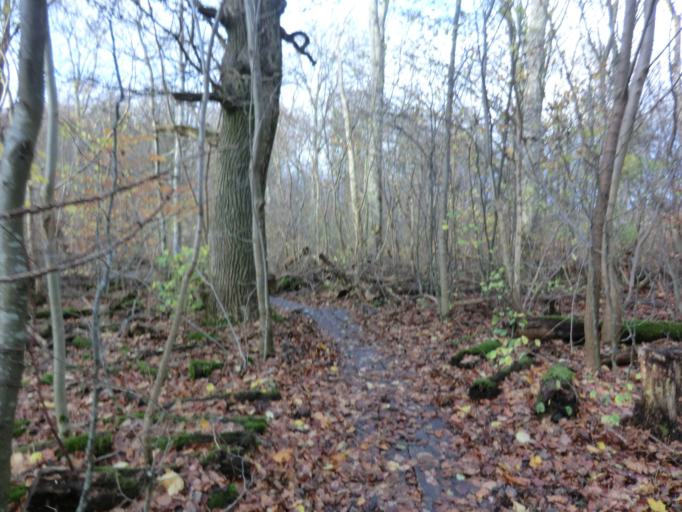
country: SE
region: Skane
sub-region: Lunds Kommun
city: Genarp
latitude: 55.6749
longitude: 13.3354
